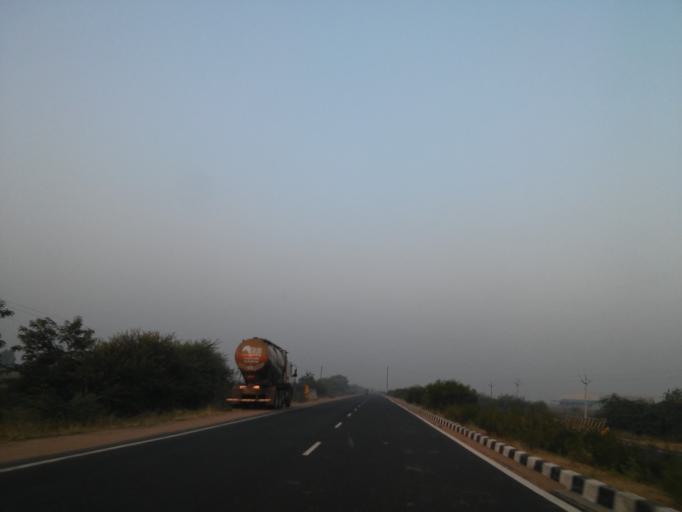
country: IN
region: Gujarat
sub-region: Surendranagar
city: Halvad
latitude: 23.0102
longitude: 71.0509
